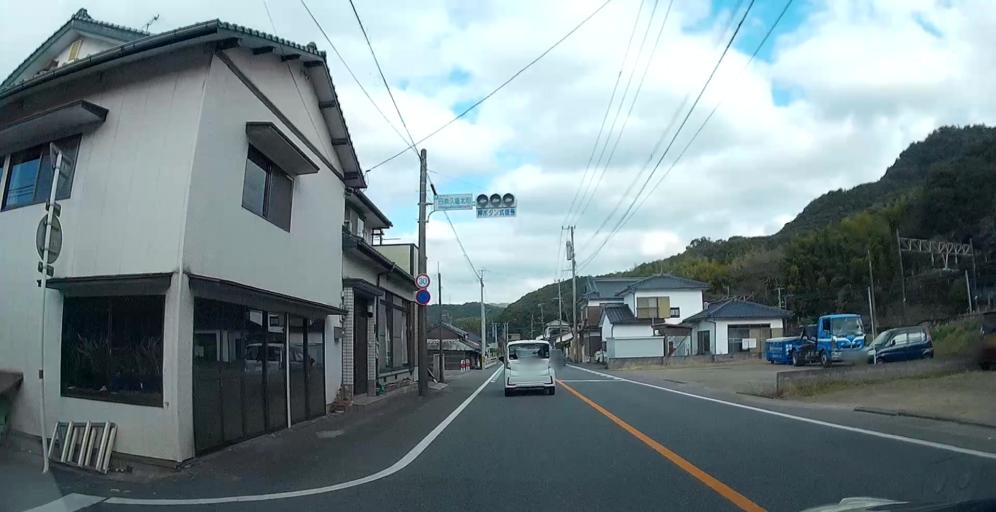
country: JP
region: Kumamoto
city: Yatsushiro
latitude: 32.4372
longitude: 130.5823
